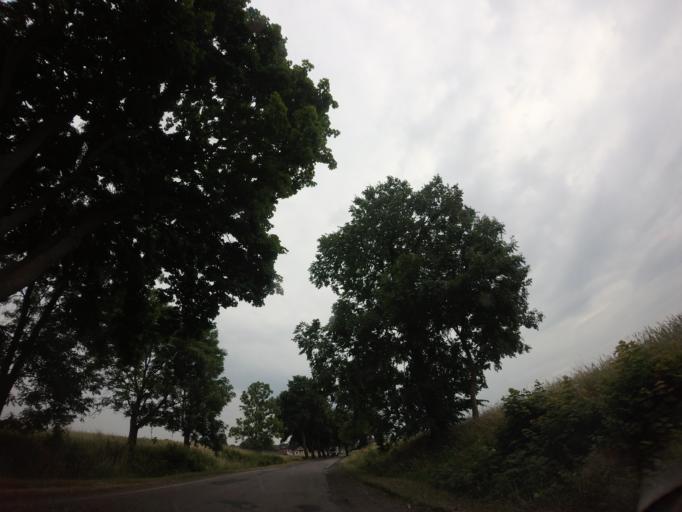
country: PL
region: West Pomeranian Voivodeship
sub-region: Powiat drawski
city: Czaplinek
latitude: 53.5392
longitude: 16.2327
